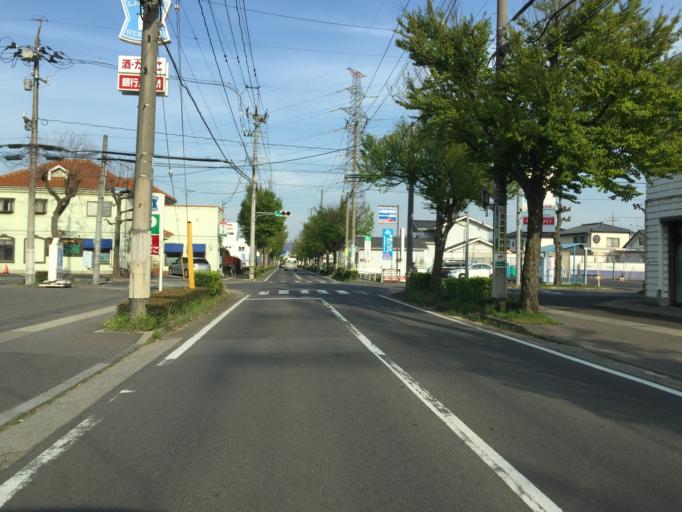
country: JP
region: Fukushima
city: Fukushima-shi
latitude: 37.7623
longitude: 140.4315
